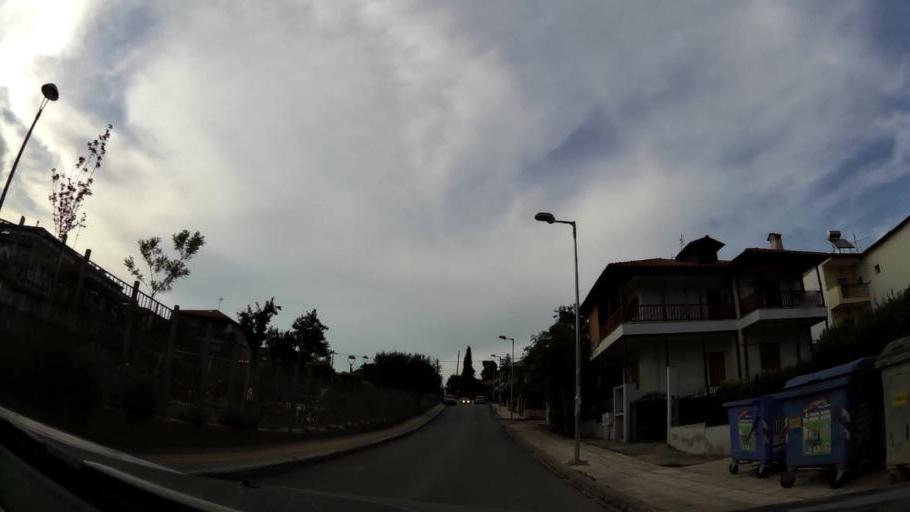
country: GR
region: Central Macedonia
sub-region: Nomos Thessalonikis
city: Pefka
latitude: 40.6575
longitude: 22.9888
